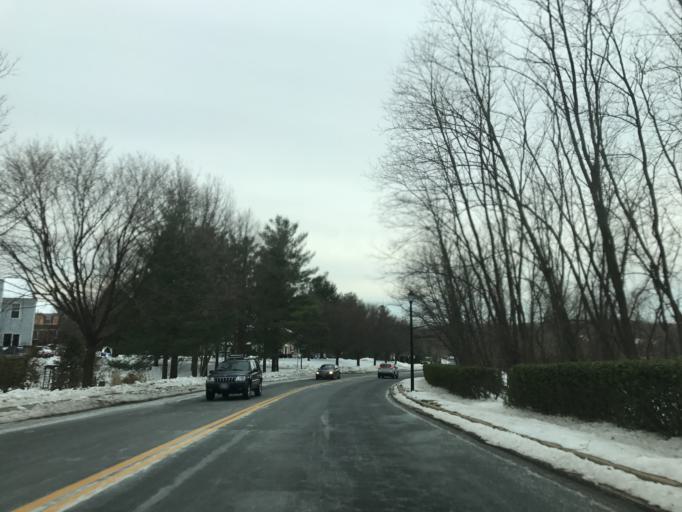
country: US
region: Maryland
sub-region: Baltimore County
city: Mays Chapel
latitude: 39.4287
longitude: -76.6461
